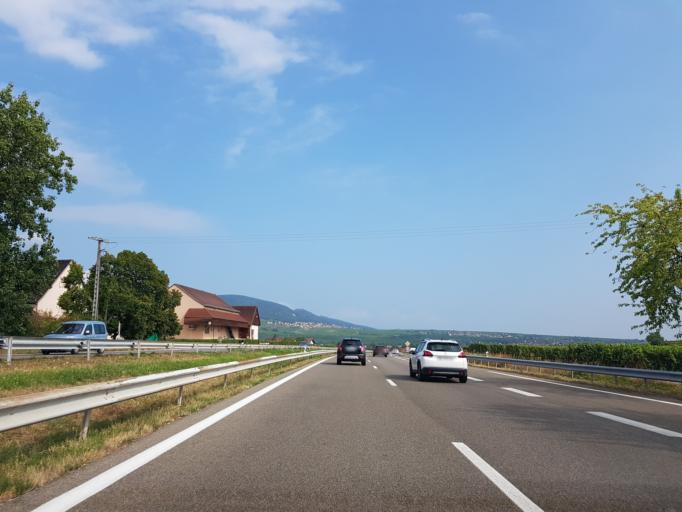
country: FR
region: Alsace
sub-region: Departement du Haut-Rhin
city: Pfaffenheim
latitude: 47.9843
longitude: 7.2931
